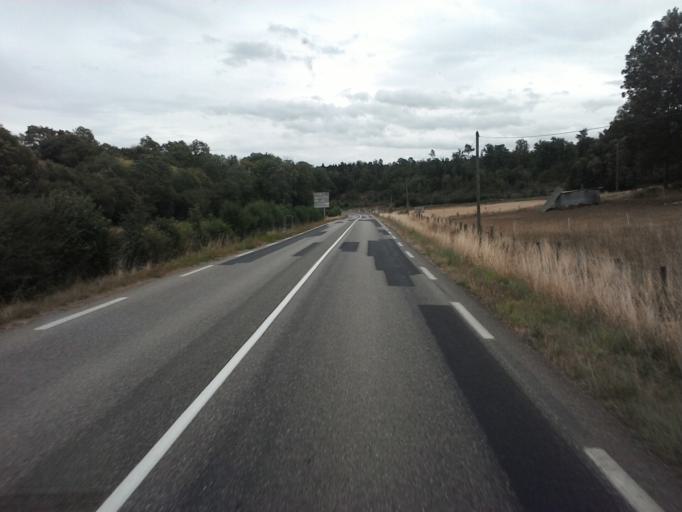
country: FR
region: Lorraine
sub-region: Departement de Meurthe-et-Moselle
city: Colombey-les-Belles
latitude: 48.5725
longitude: 5.9647
